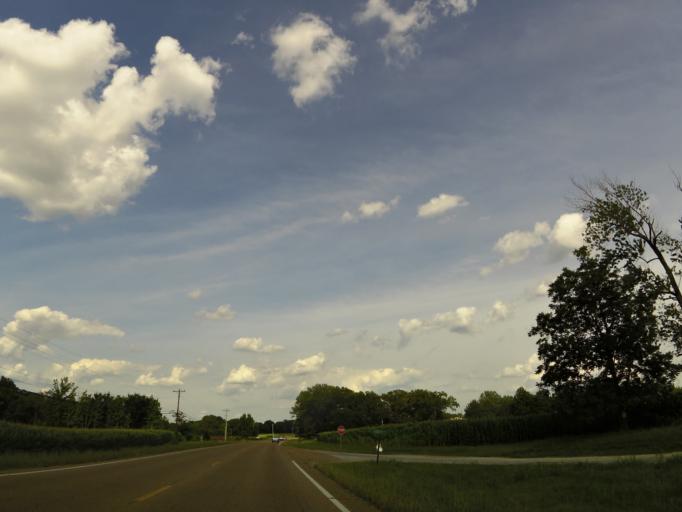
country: US
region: Tennessee
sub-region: Carroll County
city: Bruceton
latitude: 36.0380
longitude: -88.3077
